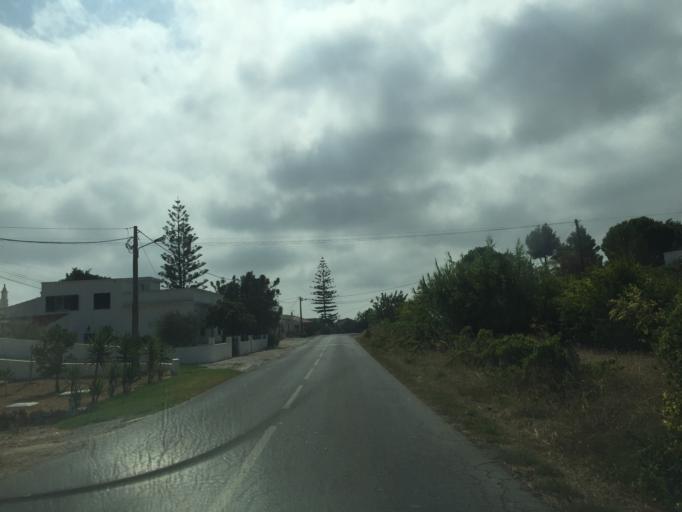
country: PT
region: Faro
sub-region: Olhao
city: Olhao
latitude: 37.0741
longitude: -7.8880
